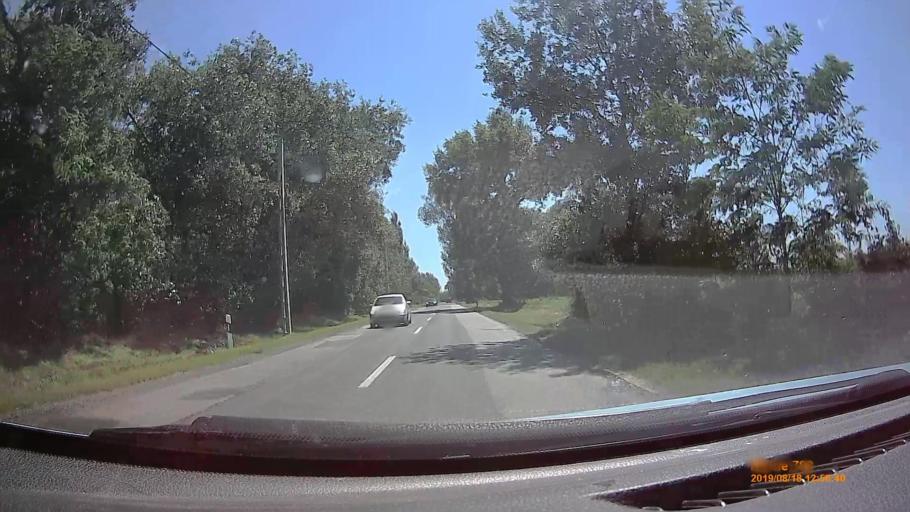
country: HU
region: Fejer
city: Sarkeresztur
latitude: 47.0221
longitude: 18.5427
